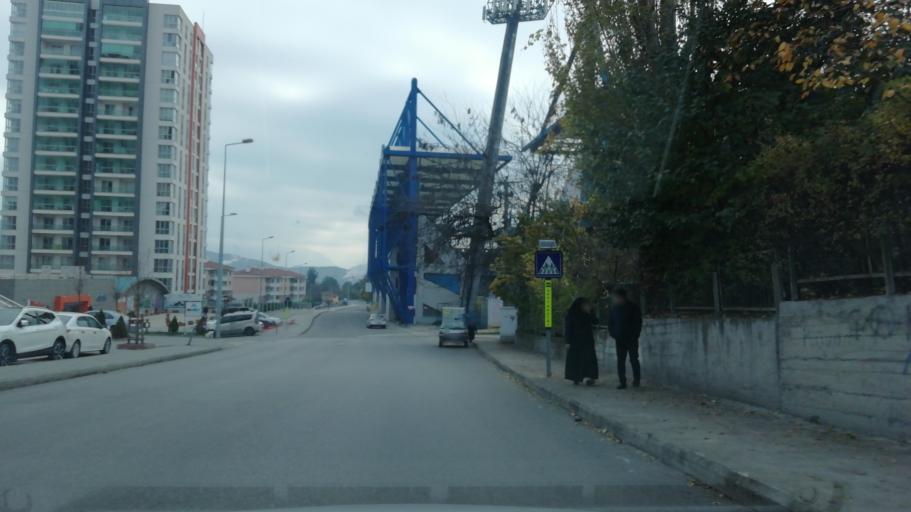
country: TR
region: Karabuk
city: Karabuk
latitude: 41.2058
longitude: 32.6202
